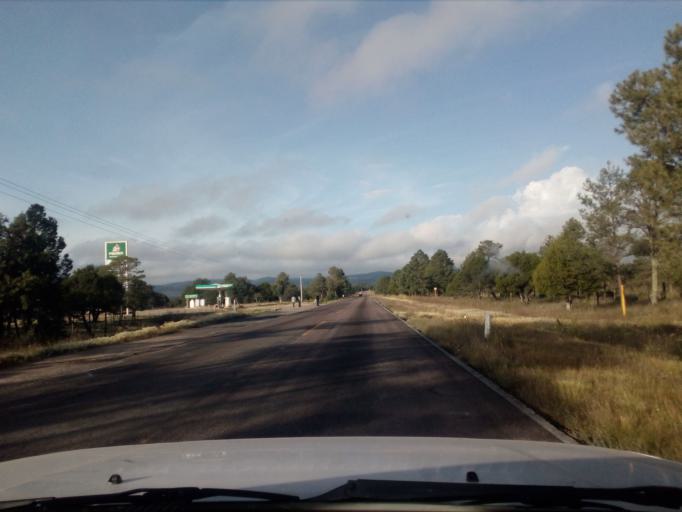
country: MX
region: Durango
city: Victoria de Durango
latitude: 23.9305
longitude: -104.9206
